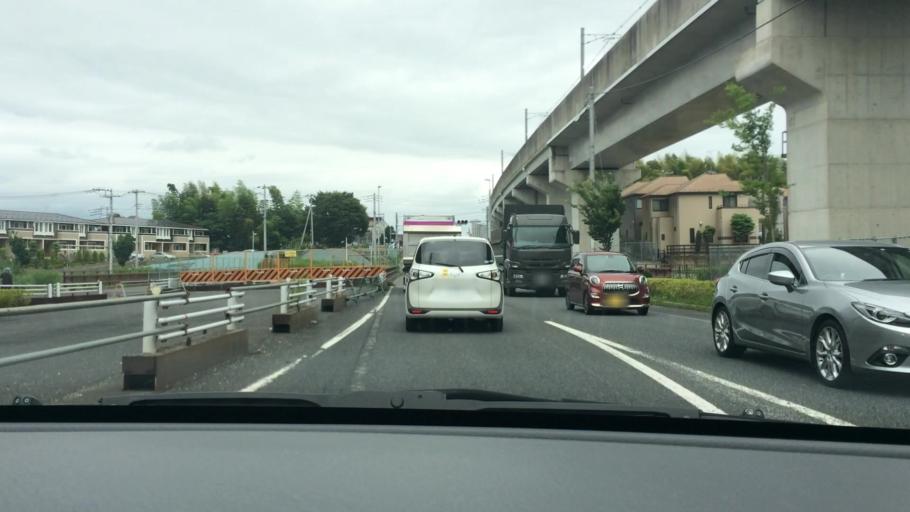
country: JP
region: Chiba
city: Nagareyama
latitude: 35.8796
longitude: 139.9334
